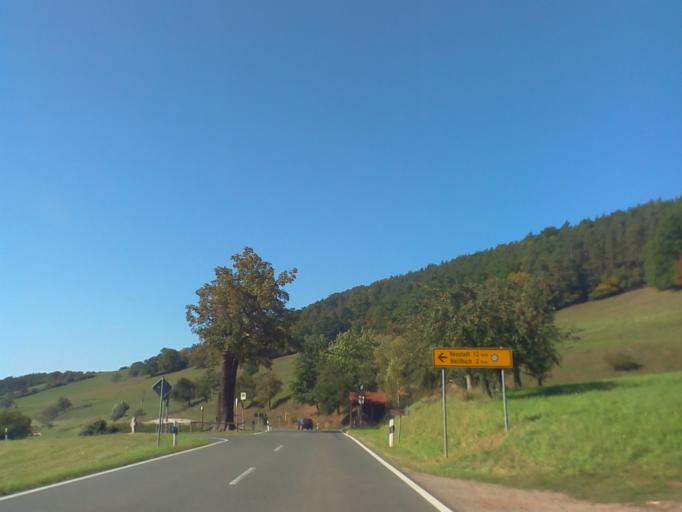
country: DE
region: Thuringia
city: Weissbach
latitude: 50.8307
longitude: 11.7907
